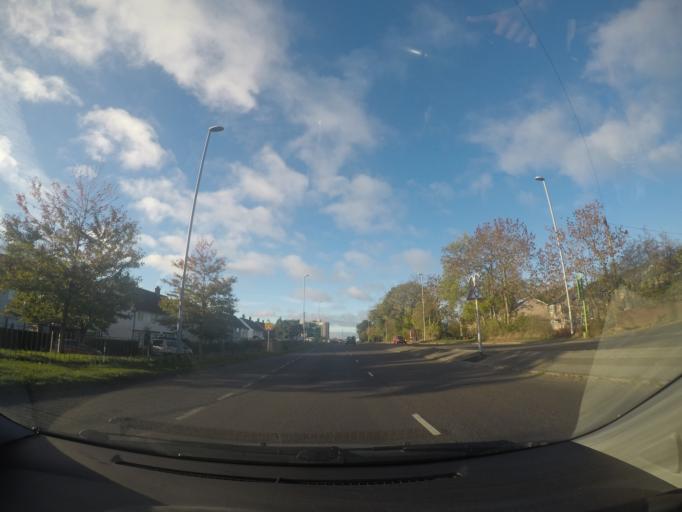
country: GB
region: England
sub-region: City and Borough of Leeds
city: Scholes
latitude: 53.8247
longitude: -1.4539
